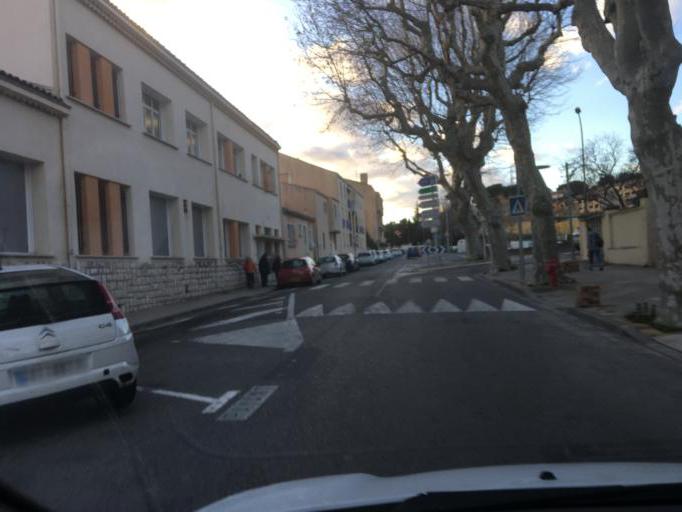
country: FR
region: Provence-Alpes-Cote d'Azur
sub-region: Departement des Bouches-du-Rhone
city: Martigues
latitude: 43.4083
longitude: 5.0523
